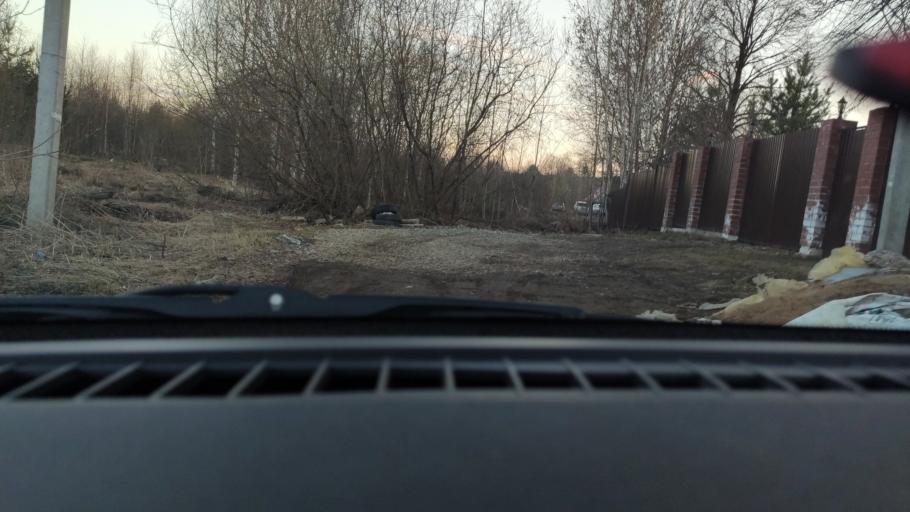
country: RU
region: Perm
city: Perm
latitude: 58.0795
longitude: 56.3170
